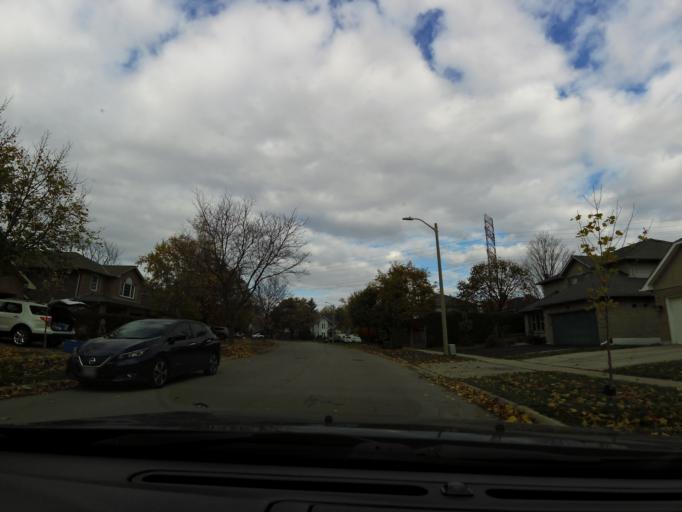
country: CA
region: Ontario
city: Burlington
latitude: 43.3273
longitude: -79.8115
